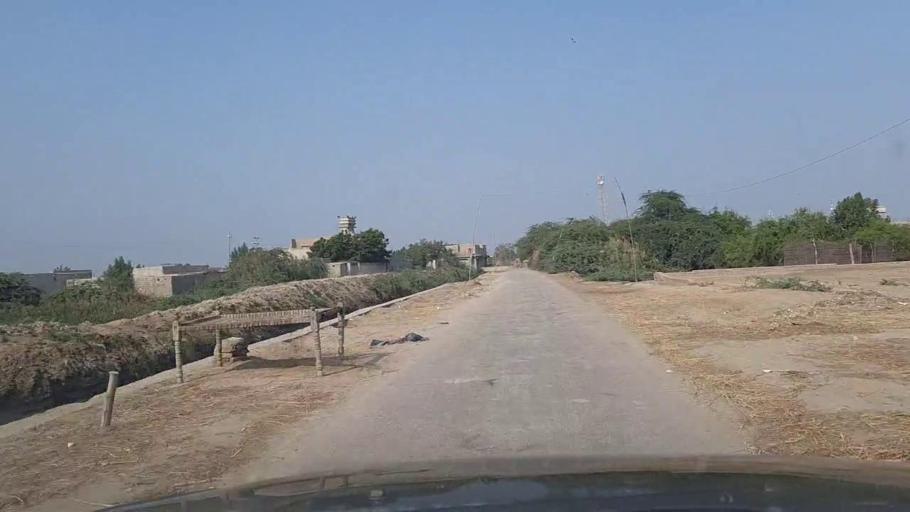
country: PK
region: Sindh
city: Mirpur Batoro
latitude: 24.7231
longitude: 68.2566
